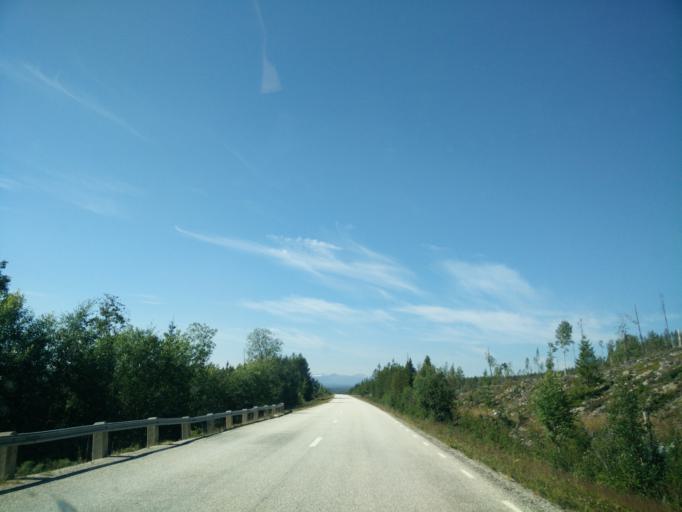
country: SE
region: Jaemtland
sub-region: Are Kommun
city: Jarpen
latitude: 62.8051
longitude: 13.5440
